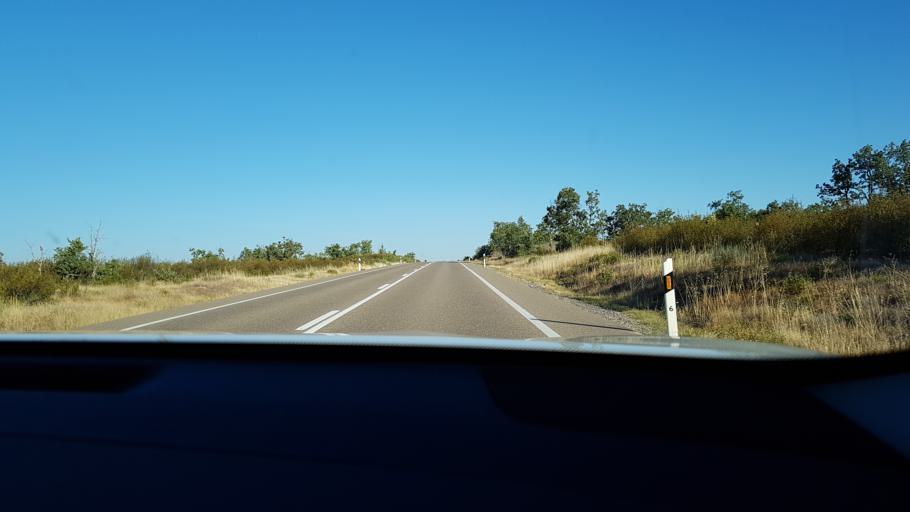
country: ES
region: Castille and Leon
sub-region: Provincia de Zamora
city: Samir de los Canos
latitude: 41.6651
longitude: -6.2156
